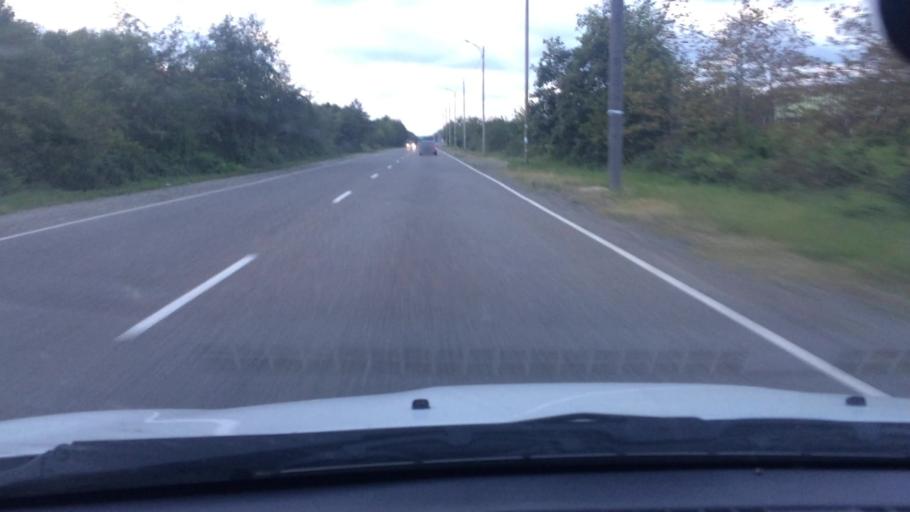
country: GE
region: Guria
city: Urek'i
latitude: 41.9337
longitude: 41.7723
